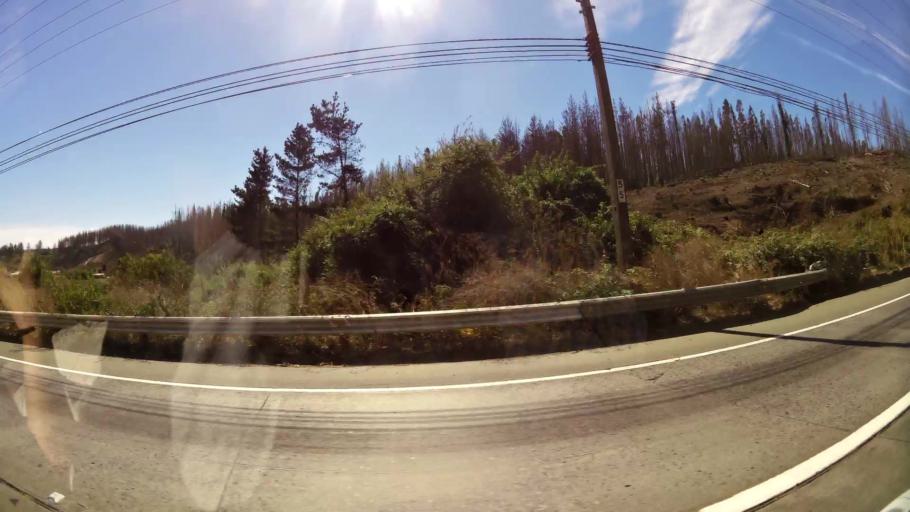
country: CL
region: Biobio
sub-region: Provincia de Concepcion
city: Penco
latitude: -36.7634
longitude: -73.0091
